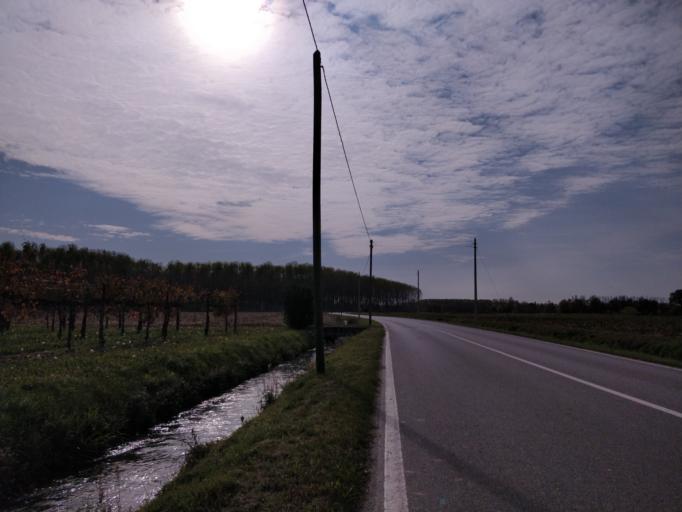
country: IT
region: Friuli Venezia Giulia
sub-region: Provincia di Udine
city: Bertiolo
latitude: 45.9349
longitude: 13.0506
